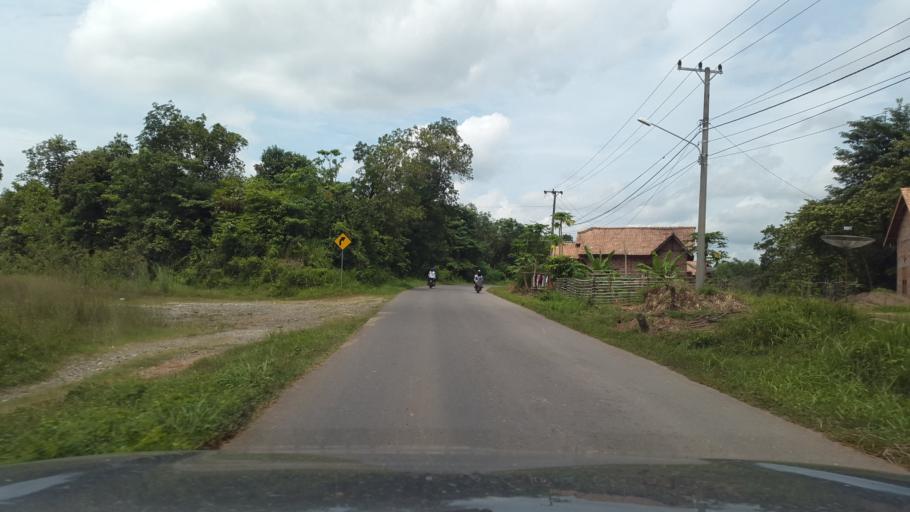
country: ID
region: South Sumatra
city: Gunungmegang Dalam
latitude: -3.3964
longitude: 103.9603
